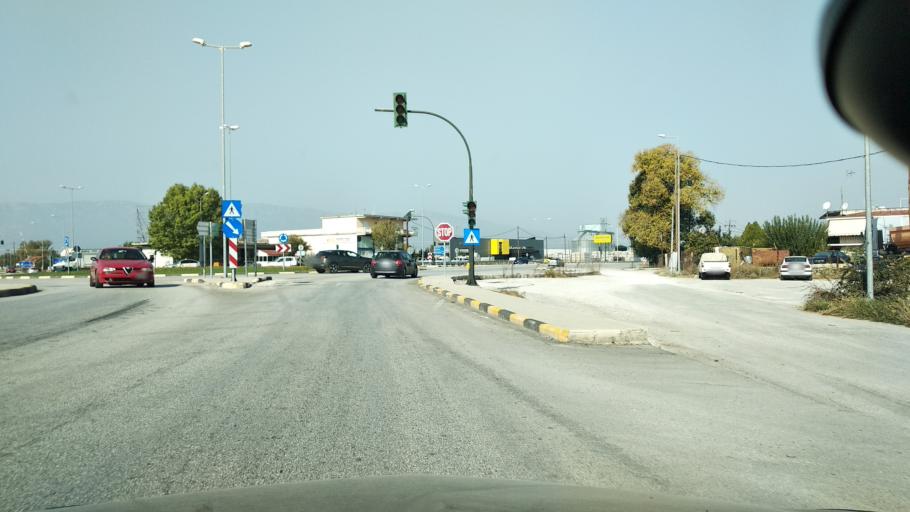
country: GR
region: Thessaly
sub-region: Trikala
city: Pyrgetos
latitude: 39.5721
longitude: 21.7480
